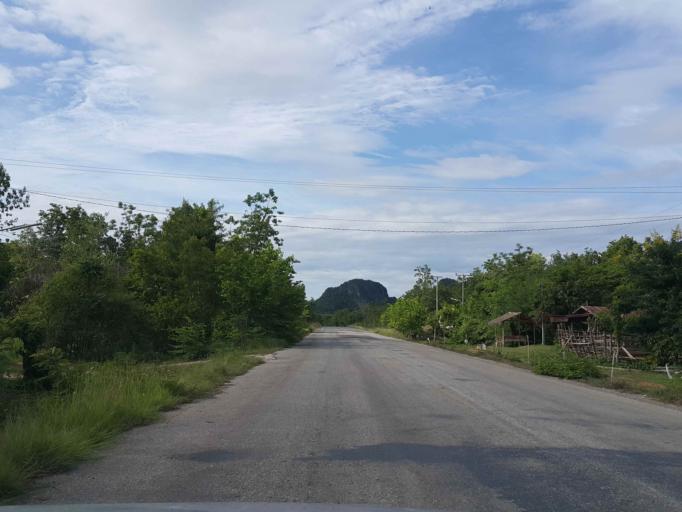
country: TH
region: Sukhothai
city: Thung Saliam
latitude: 17.2985
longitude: 99.5270
